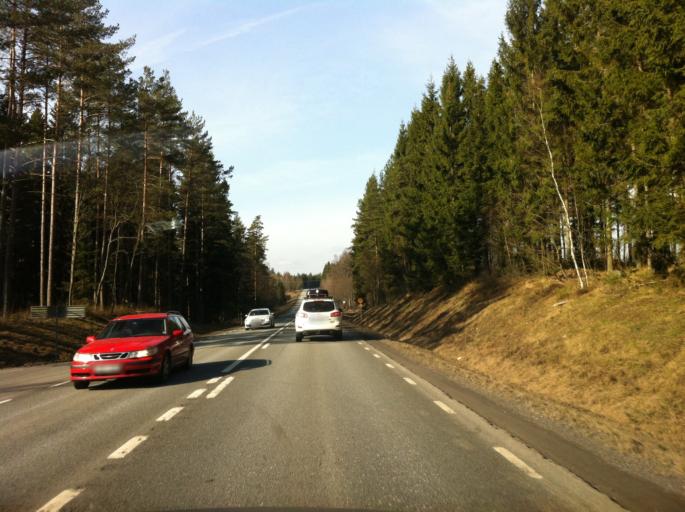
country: SE
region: Joenkoeping
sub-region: Jonkopings Kommun
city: Bankeryd
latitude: 57.8427
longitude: 14.0483
